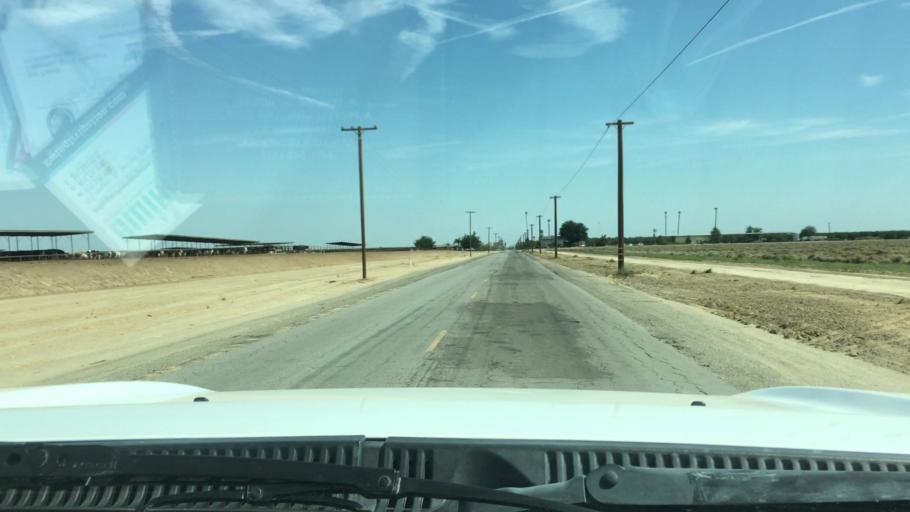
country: US
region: California
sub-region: Kern County
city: Buttonwillow
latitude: 35.4158
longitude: -119.3765
